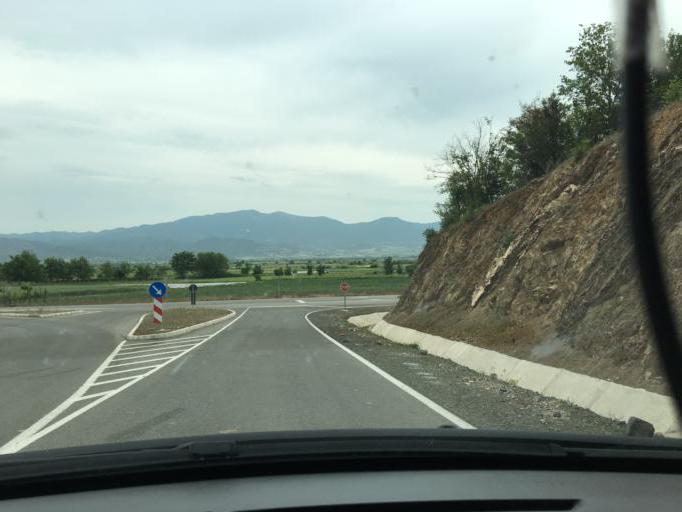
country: MK
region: Gevgelija
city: Miravci
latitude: 41.3035
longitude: 22.4432
